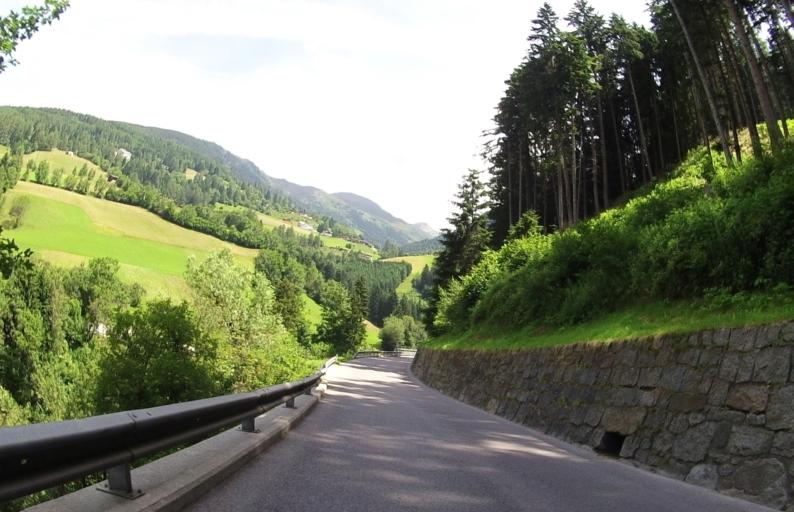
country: AT
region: Tyrol
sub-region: Politischer Bezirk Innsbruck Land
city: Ellbogen
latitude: 47.1616
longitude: 11.4573
